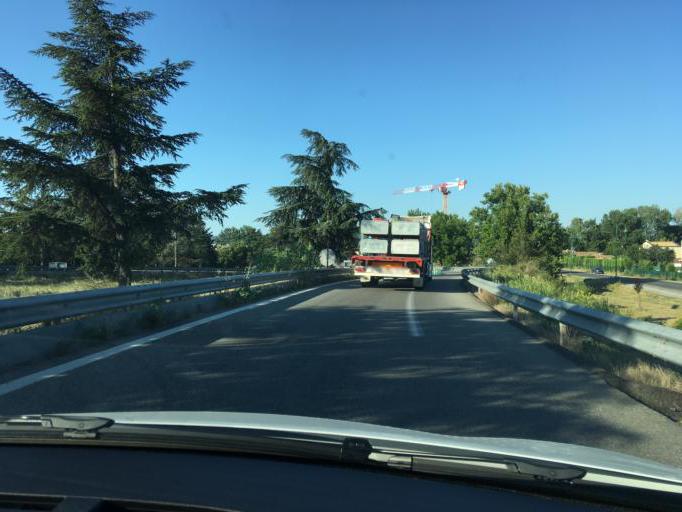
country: FR
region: Provence-Alpes-Cote d'Azur
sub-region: Departement des Bouches-du-Rhone
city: Senas
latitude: 43.7454
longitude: 5.0855
